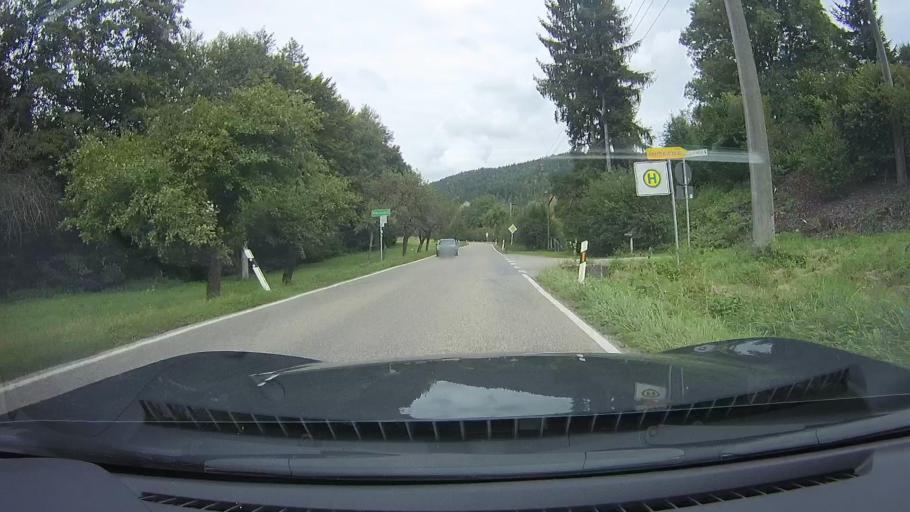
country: DE
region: Baden-Wuerttemberg
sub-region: Regierungsbezirk Stuttgart
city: Kaisersbach
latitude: 48.9598
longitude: 9.6419
